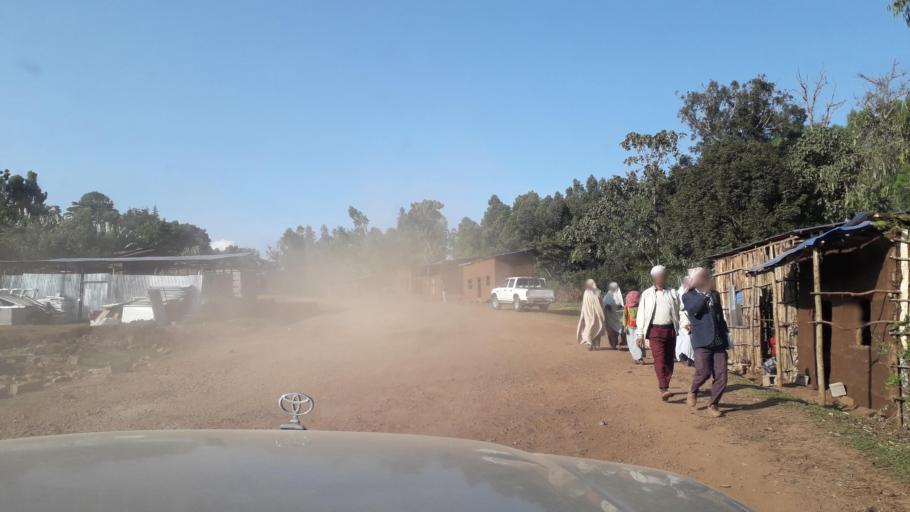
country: ET
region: Oromiya
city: Jima
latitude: 7.4880
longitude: 36.8805
